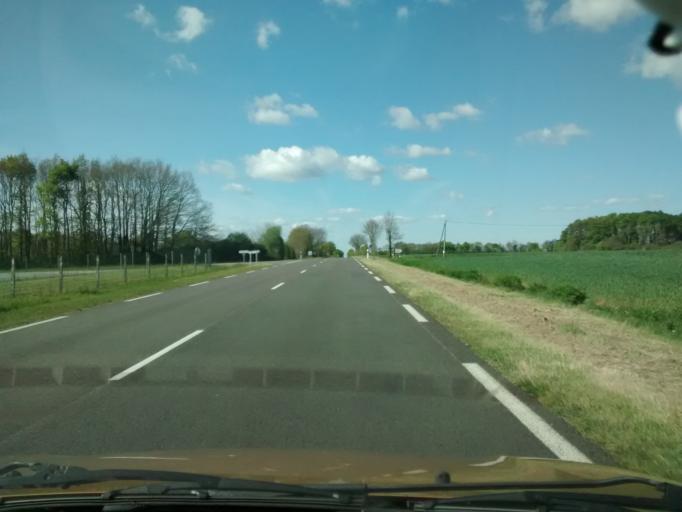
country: FR
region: Pays de la Loire
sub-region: Departement de la Vendee
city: Les Lucs-sur-Boulogne
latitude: 46.8779
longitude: -1.5001
